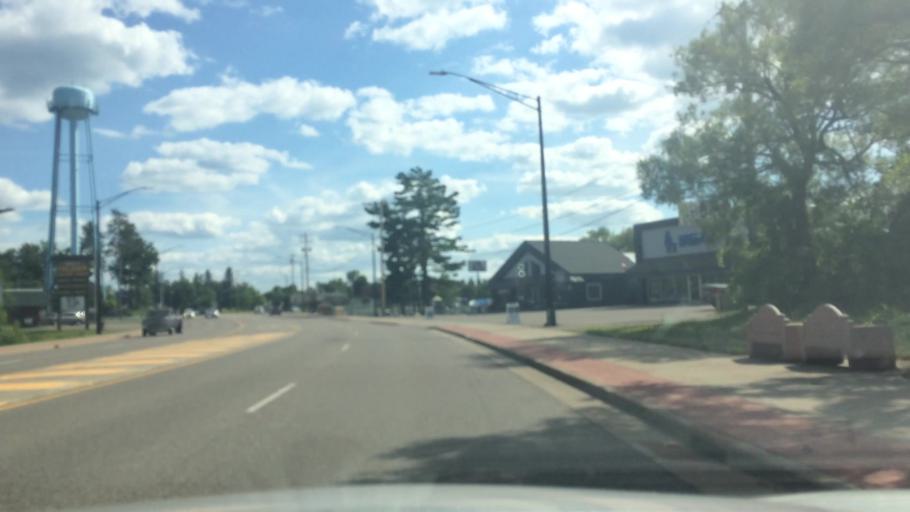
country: US
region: Wisconsin
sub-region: Vilas County
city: Lac du Flambeau
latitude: 45.8748
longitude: -89.7066
